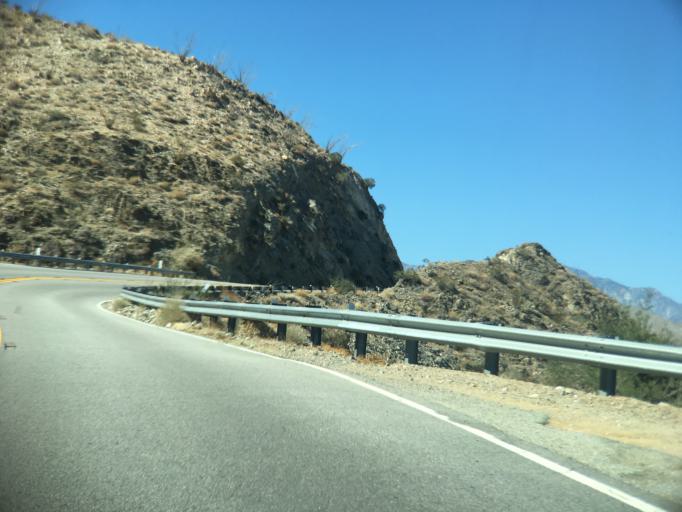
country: US
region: California
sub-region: Riverside County
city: Palm Desert
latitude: 33.6504
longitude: -116.3970
